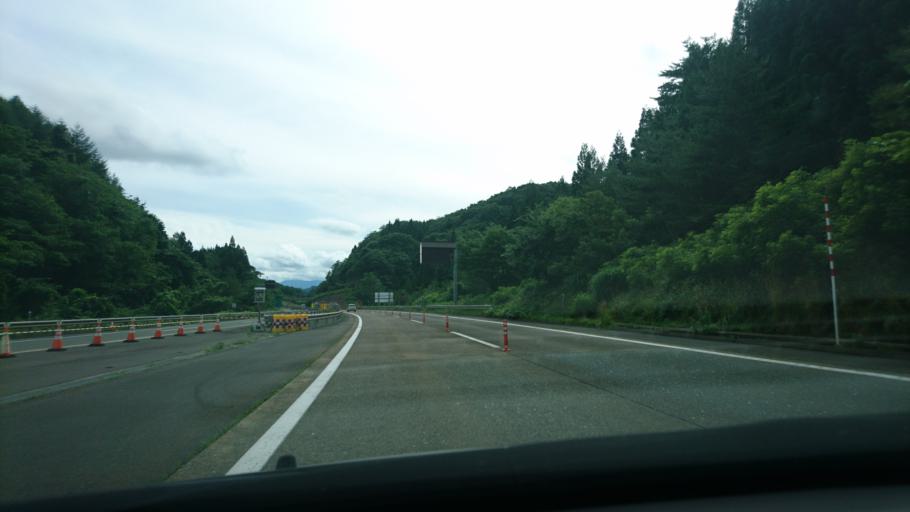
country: JP
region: Iwate
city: Ichinohe
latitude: 40.2292
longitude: 141.3721
